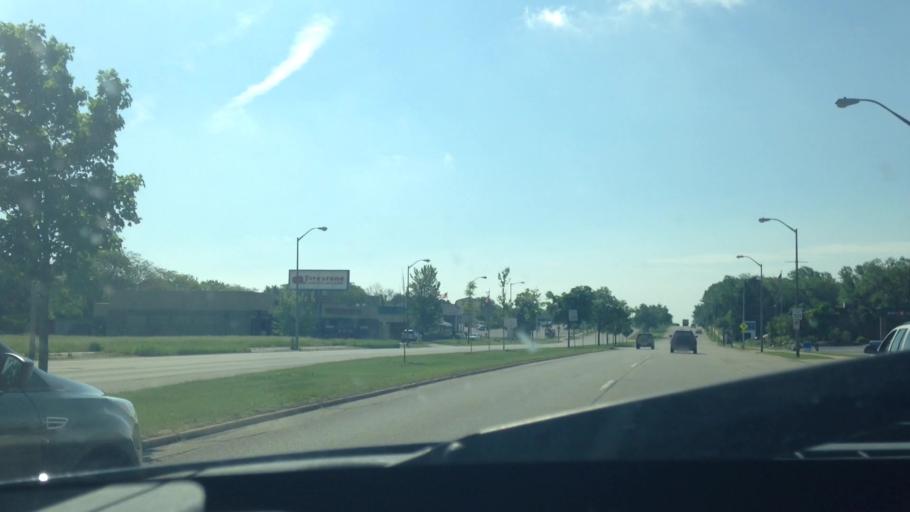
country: US
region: Wisconsin
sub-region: Waukesha County
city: Menomonee Falls
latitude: 43.1686
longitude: -88.1026
